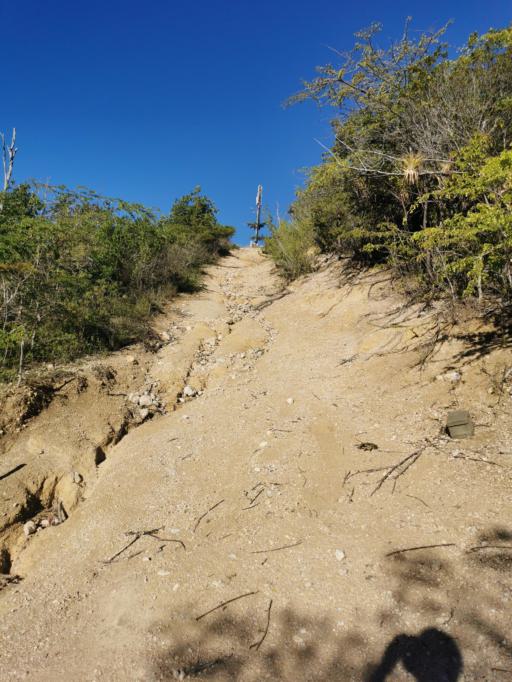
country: AG
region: Saint John
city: Saint John's
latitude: 17.1378
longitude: -61.8242
